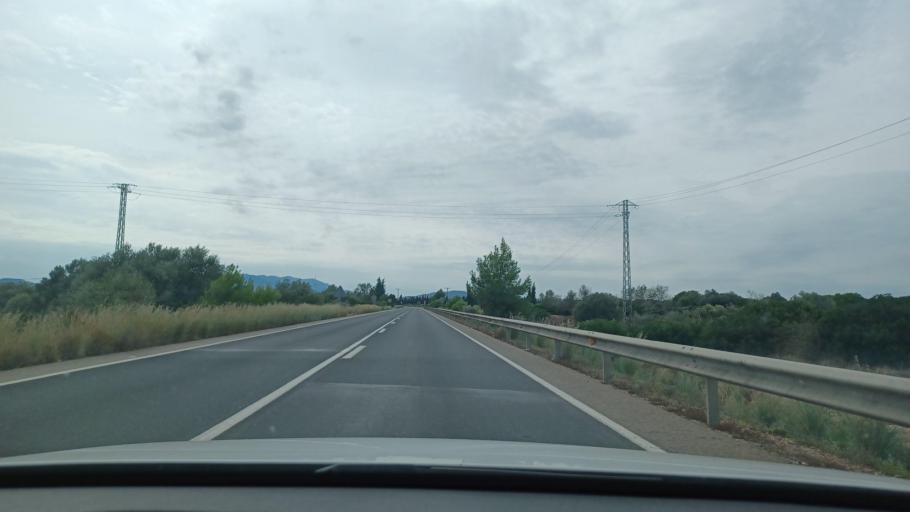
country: ES
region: Catalonia
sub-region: Provincia de Tarragona
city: Santa Barbara
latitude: 40.7597
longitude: 0.5019
